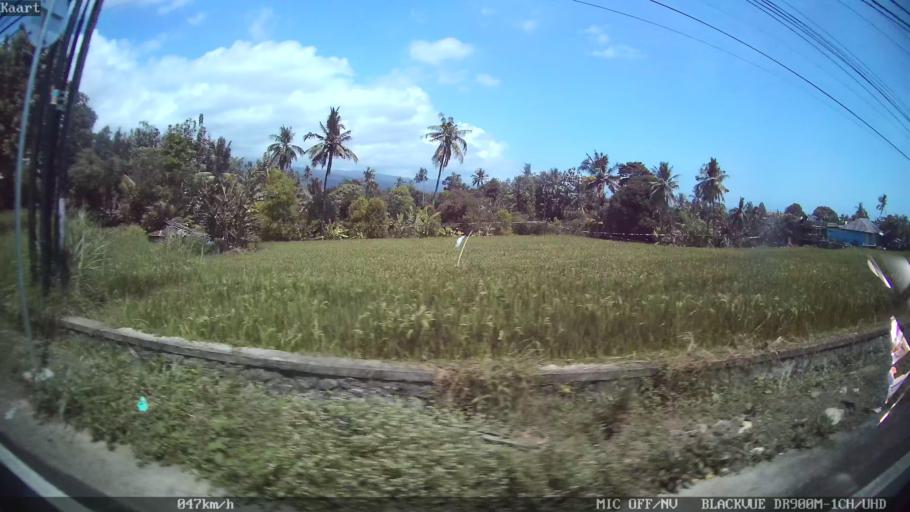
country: ID
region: Bali
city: Banjar Dajanmargi
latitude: -8.1551
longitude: 115.1109
